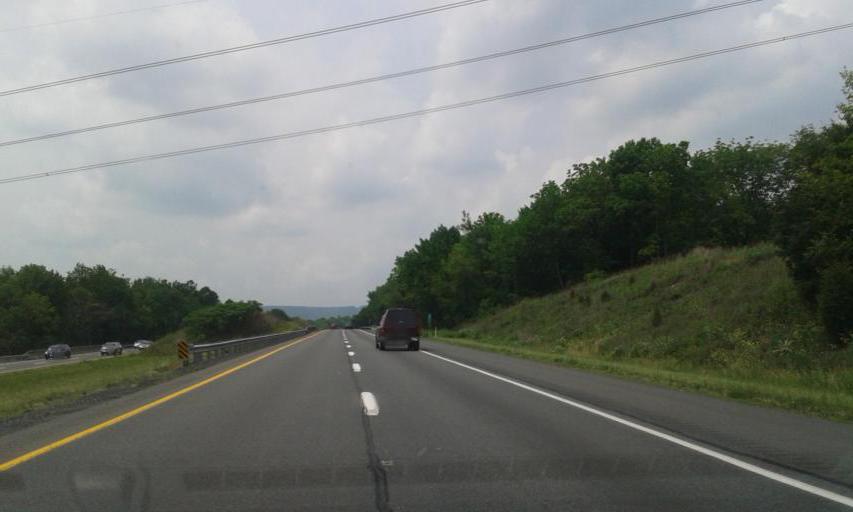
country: US
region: Pennsylvania
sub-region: Northampton County
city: Belfast
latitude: 40.7977
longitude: -75.2928
